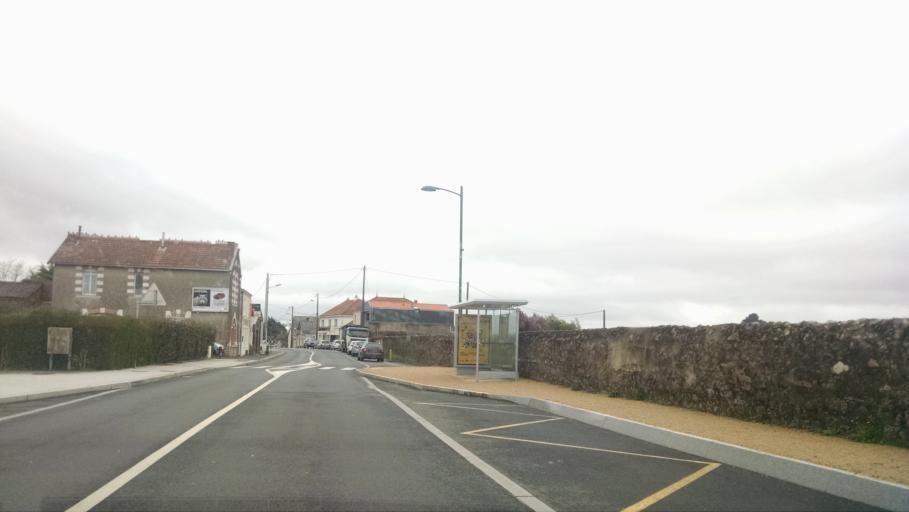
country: FR
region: Pays de la Loire
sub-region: Departement de la Loire-Atlantique
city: Monnieres
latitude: 47.1436
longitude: -1.3472
